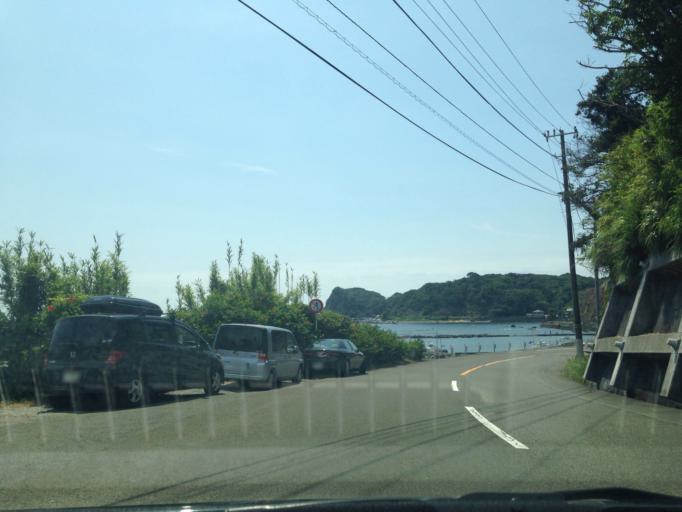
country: JP
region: Shizuoka
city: Shimoda
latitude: 34.6246
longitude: 138.8815
